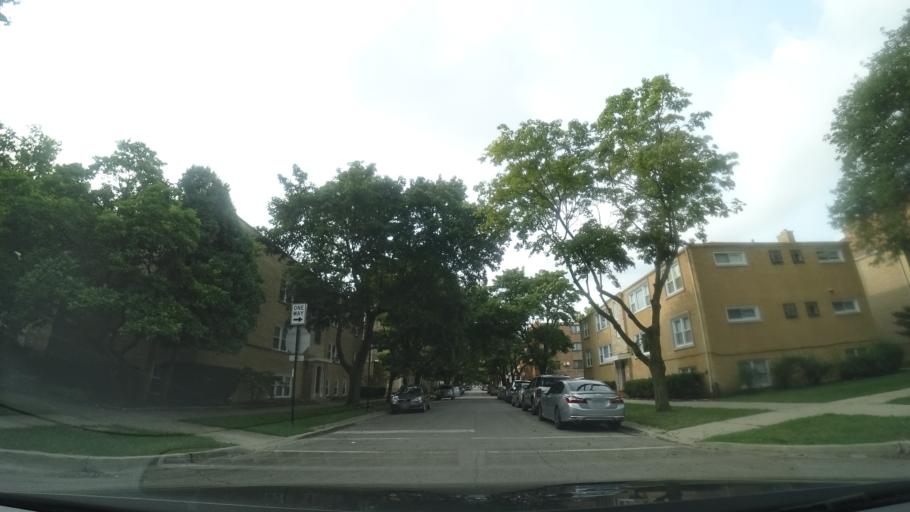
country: US
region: Illinois
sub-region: Cook County
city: Evanston
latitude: 42.0095
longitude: -87.6974
